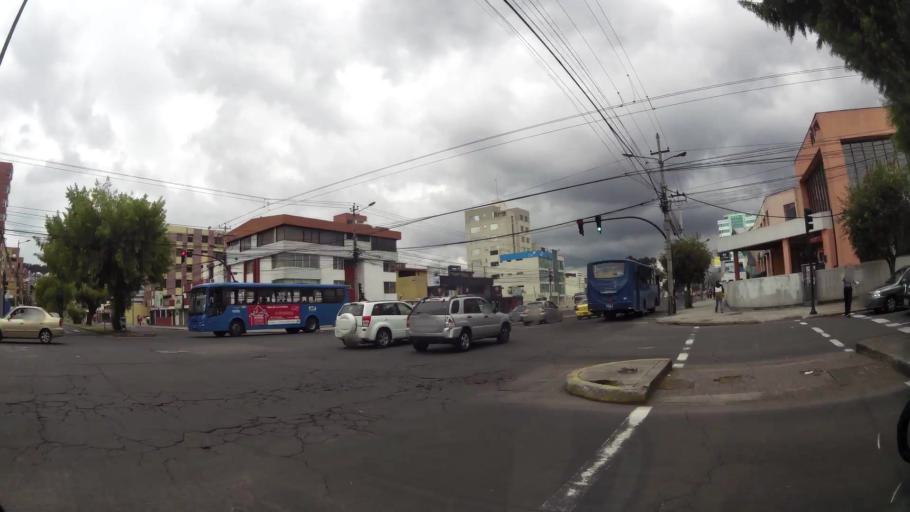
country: EC
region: Pichincha
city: Quito
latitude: -0.1702
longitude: -78.4800
